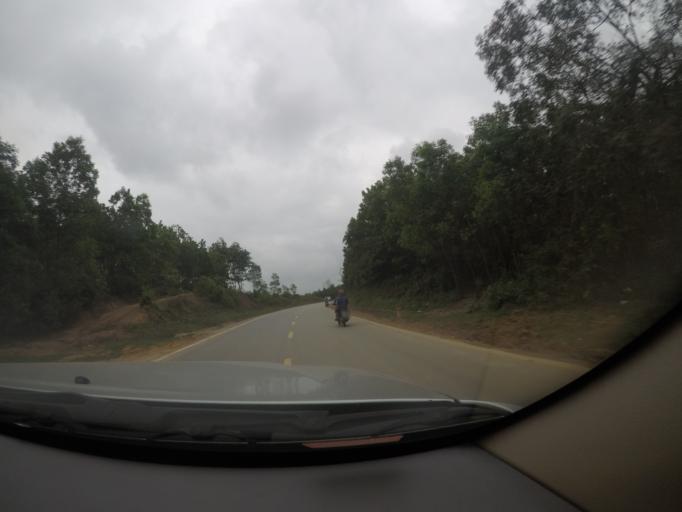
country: VN
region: Quang Tri
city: Cam Lo
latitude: 16.8378
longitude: 107.0000
